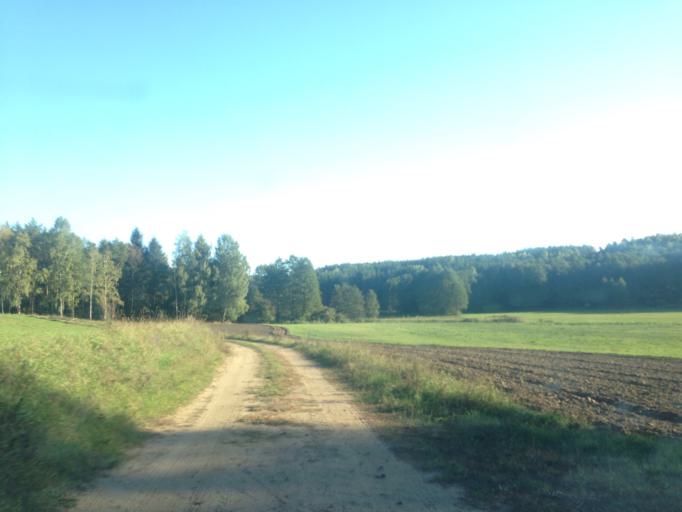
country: PL
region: Kujawsko-Pomorskie
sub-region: Powiat brodnicki
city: Bartniczka
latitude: 53.2765
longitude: 19.6231
